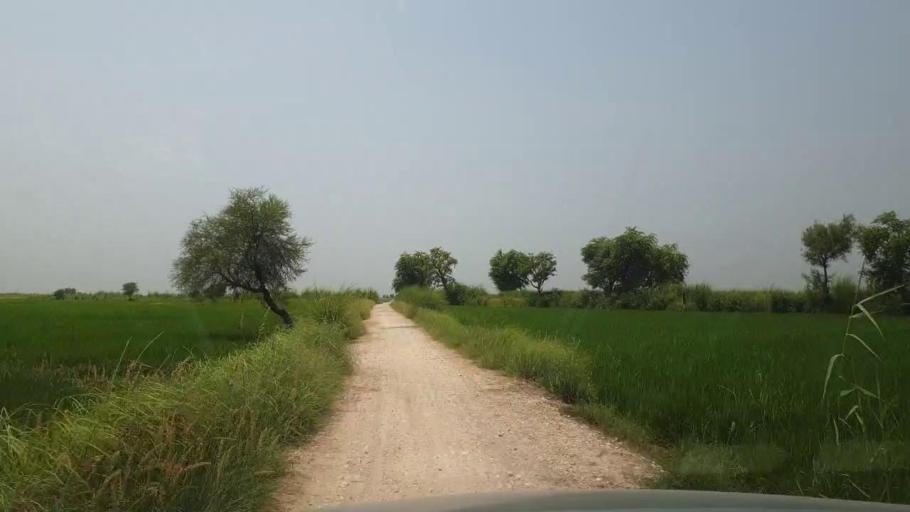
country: PK
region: Sindh
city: Garhi Yasin
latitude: 27.8706
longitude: 68.4904
